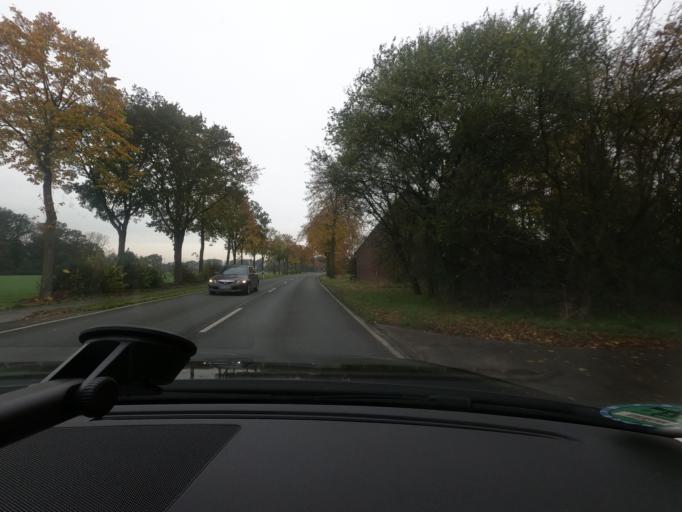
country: DE
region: North Rhine-Westphalia
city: Geldern
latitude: 51.5321
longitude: 6.2919
